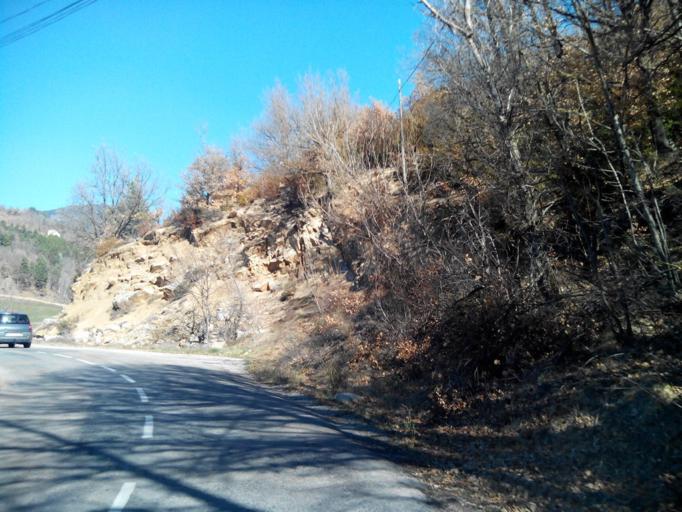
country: ES
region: Catalonia
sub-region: Provincia de Lleida
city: Lles de Cerdanya
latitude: 42.3666
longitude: 1.6846
